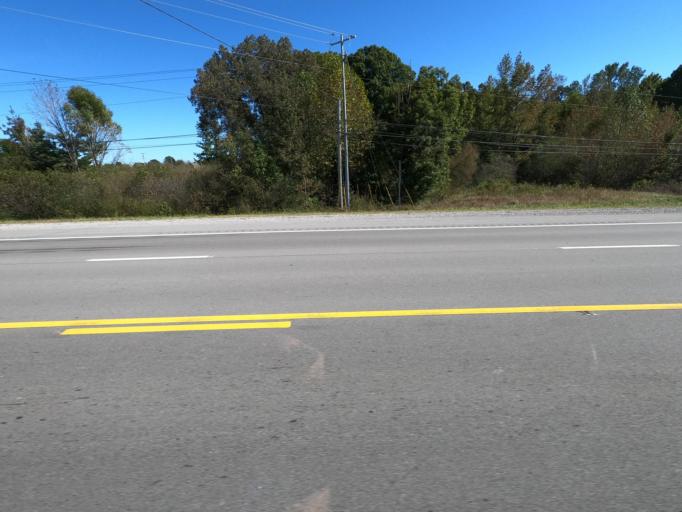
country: US
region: Tennessee
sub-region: Maury County
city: Mount Pleasant
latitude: 35.4264
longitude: -87.2818
